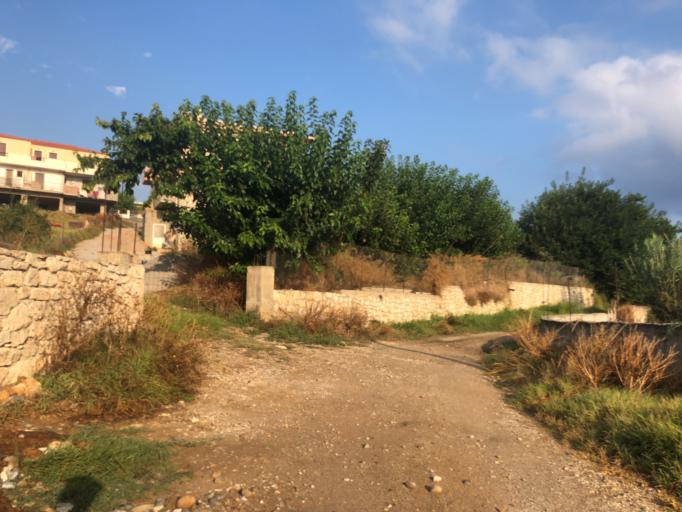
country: GR
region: Crete
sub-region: Nomos Chanias
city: Georgioupolis
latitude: 35.3456
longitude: 24.3127
